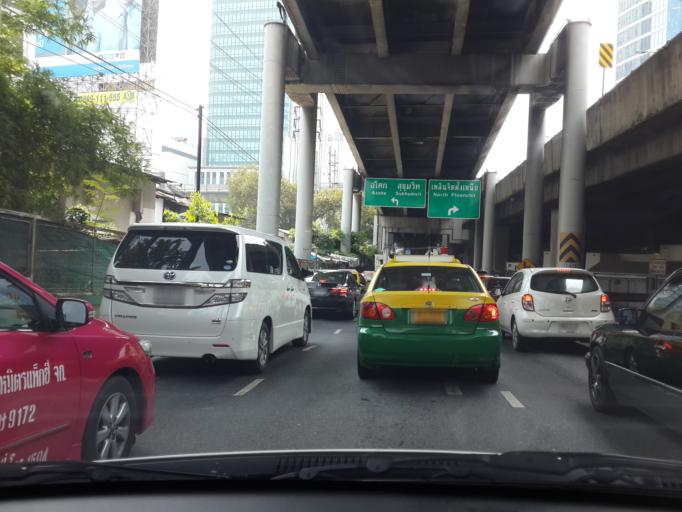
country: TH
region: Bangkok
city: Ratchathewi
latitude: 13.7438
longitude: 100.5505
